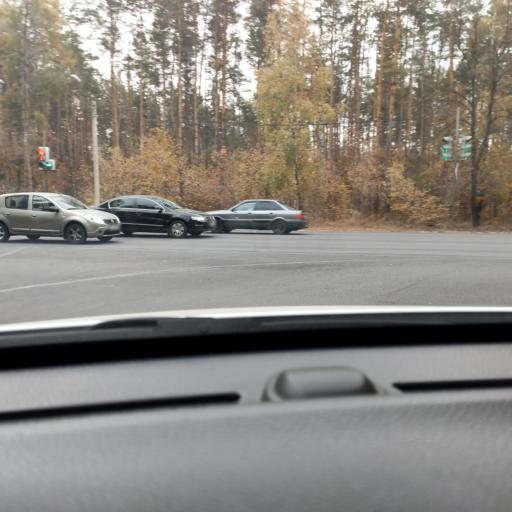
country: RU
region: Voronezj
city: Voronezh
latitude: 51.6843
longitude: 39.2825
